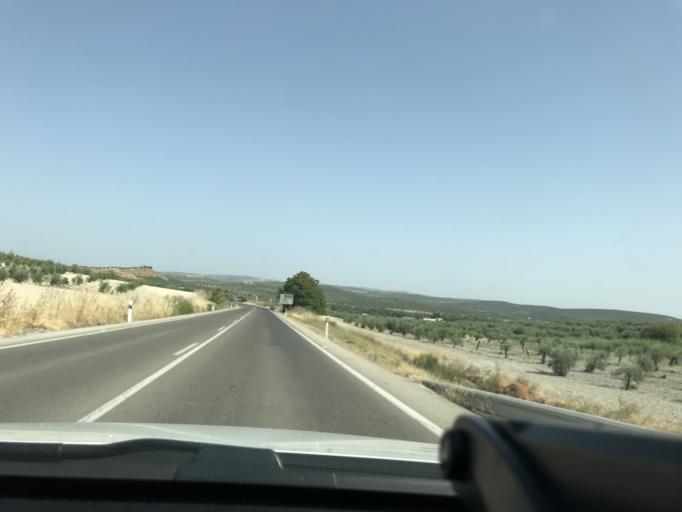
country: ES
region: Andalusia
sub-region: Provincia de Jaen
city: Peal de Becerro
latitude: 37.9539
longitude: -3.1780
